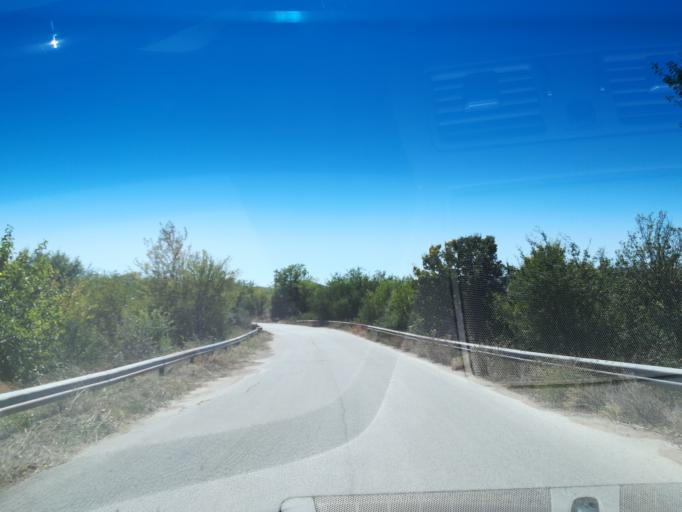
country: BG
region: Pazardzhik
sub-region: Obshtina Strelcha
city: Strelcha
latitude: 42.3580
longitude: 24.3993
